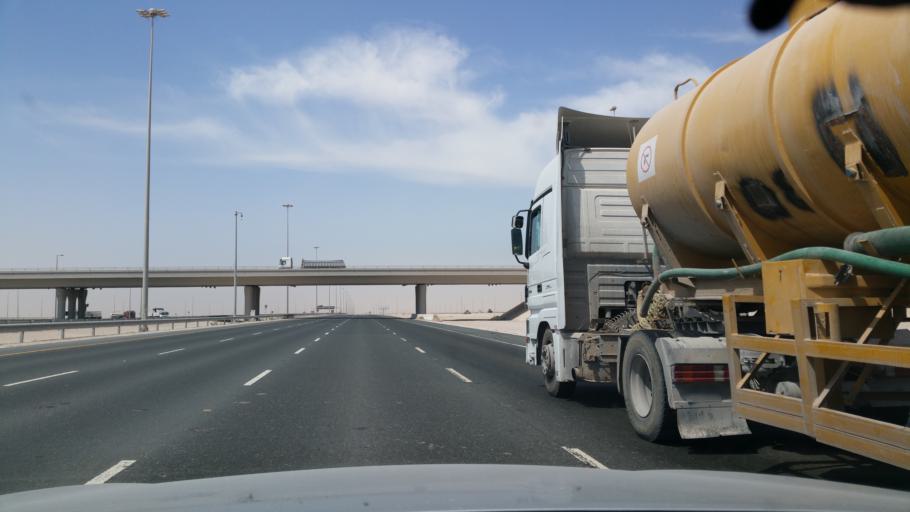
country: QA
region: Baladiyat ar Rayyan
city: Ash Shahaniyah
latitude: 25.1096
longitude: 51.1686
